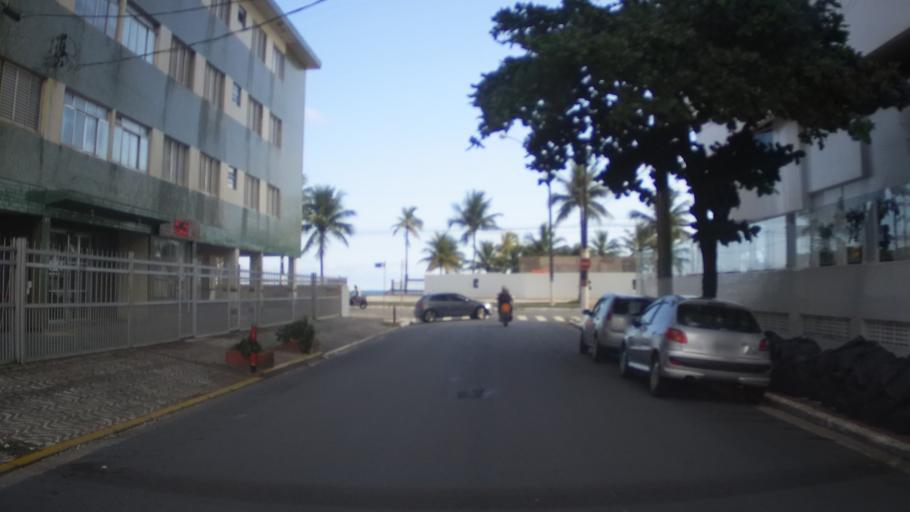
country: BR
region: Sao Paulo
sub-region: Praia Grande
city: Praia Grande
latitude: -24.0146
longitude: -46.4038
